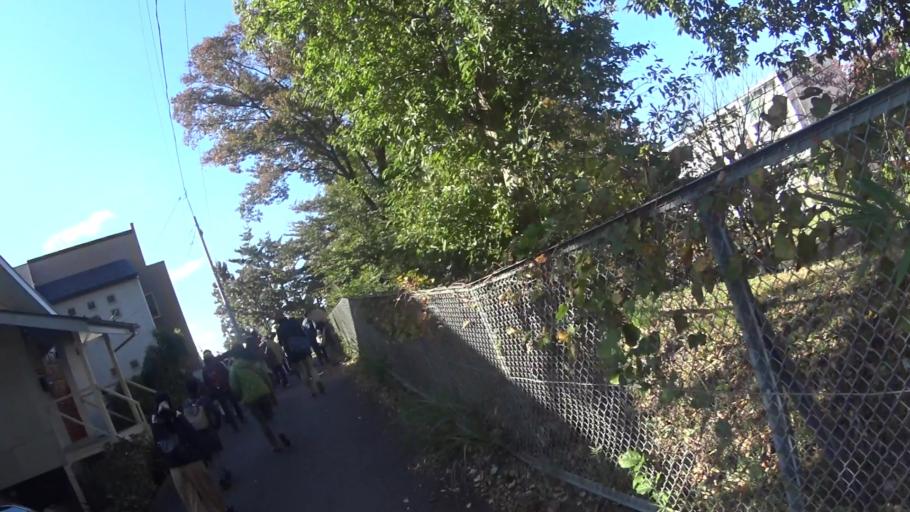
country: JP
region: Tokyo
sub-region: Machida-shi
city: Machida
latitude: 35.6087
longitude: 139.4855
